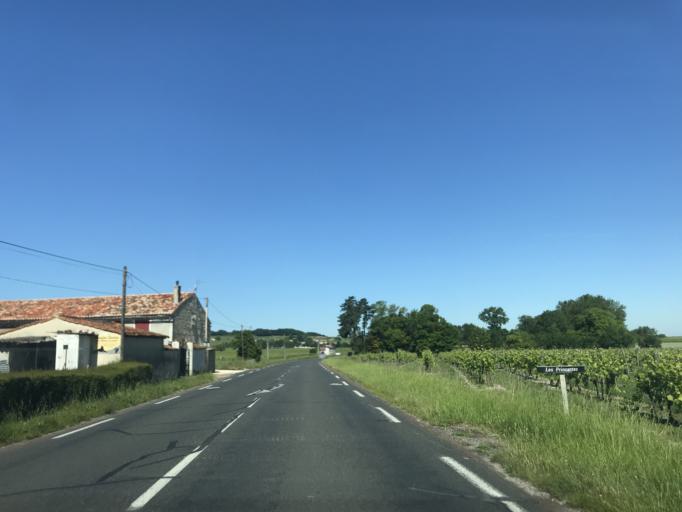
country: FR
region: Poitou-Charentes
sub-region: Departement de la Charente
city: Barbezieux-Saint-Hilaire
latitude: 45.5074
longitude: -0.2639
